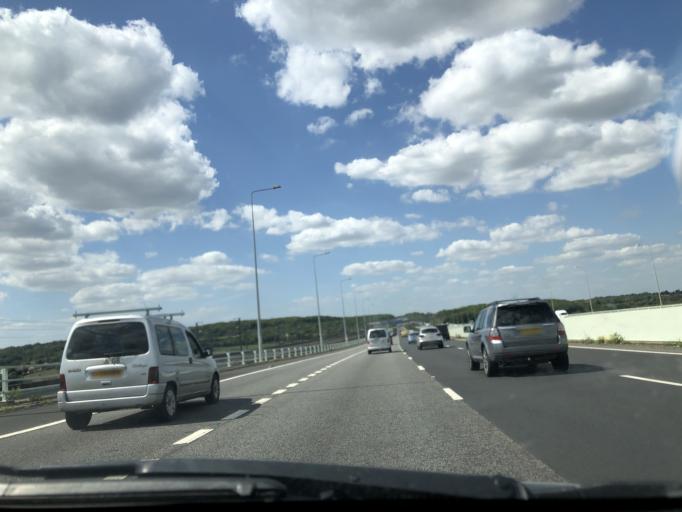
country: GB
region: England
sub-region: Medway
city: Cuxton
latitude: 51.3737
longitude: 0.4774
